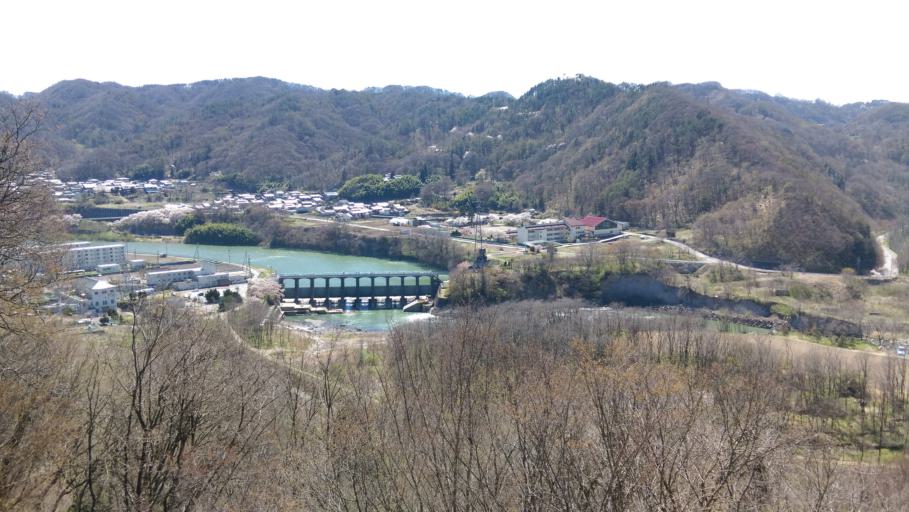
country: JP
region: Nagano
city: Komoro
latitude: 36.3274
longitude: 138.4162
